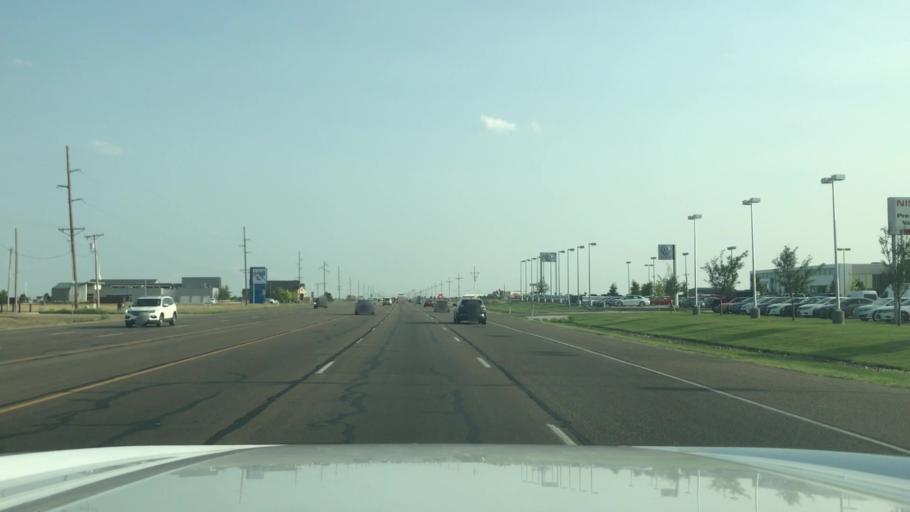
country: US
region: Texas
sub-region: Potter County
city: Amarillo
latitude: 35.1590
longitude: -101.9383
